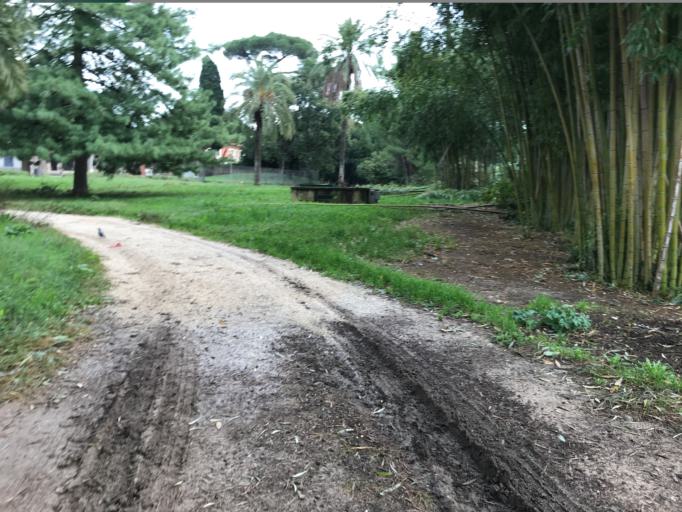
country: IT
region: Latium
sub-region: Citta metropolitana di Roma Capitale
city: Rome
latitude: 41.9139
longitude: 12.5120
